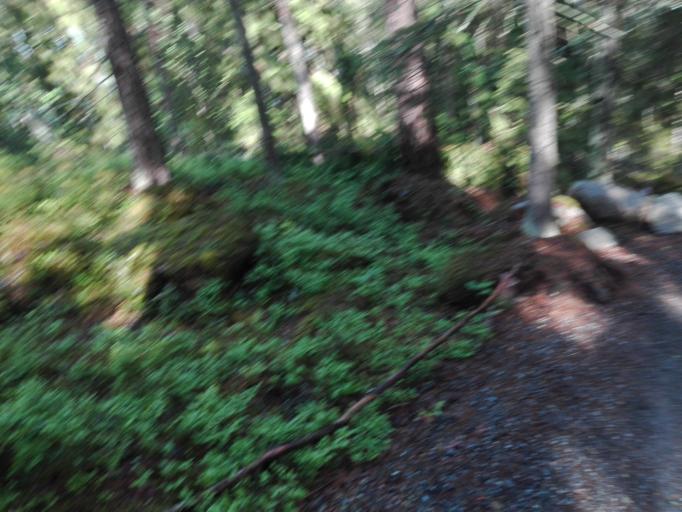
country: SE
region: Stockholm
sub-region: Nacka Kommun
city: Fisksatra
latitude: 59.2947
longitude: 18.2713
